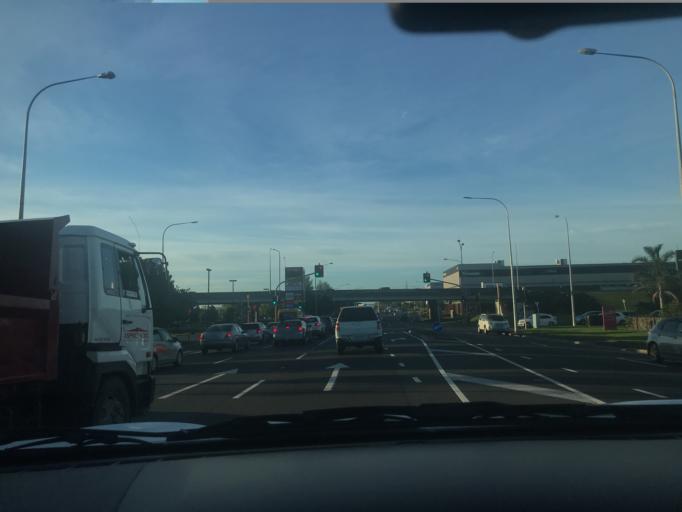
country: NZ
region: Auckland
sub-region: Auckland
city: Tamaki
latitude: -36.9143
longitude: 174.8388
